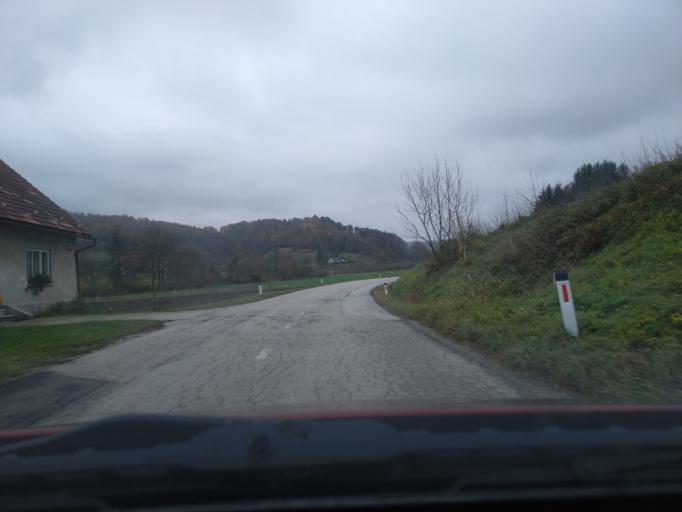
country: SI
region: Kungota
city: Zgornja Kungota
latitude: 46.6572
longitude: 15.6119
